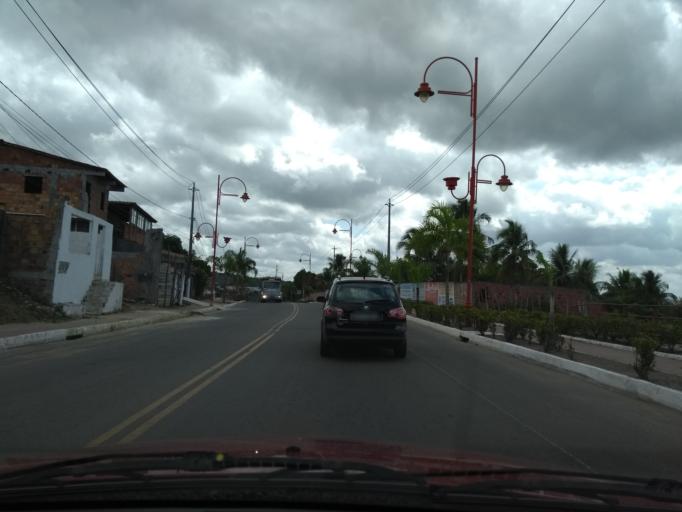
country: BR
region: Bahia
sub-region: Sao Francisco Do Conde
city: Sao Francisco do Conde
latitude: -12.6204
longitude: -38.6709
